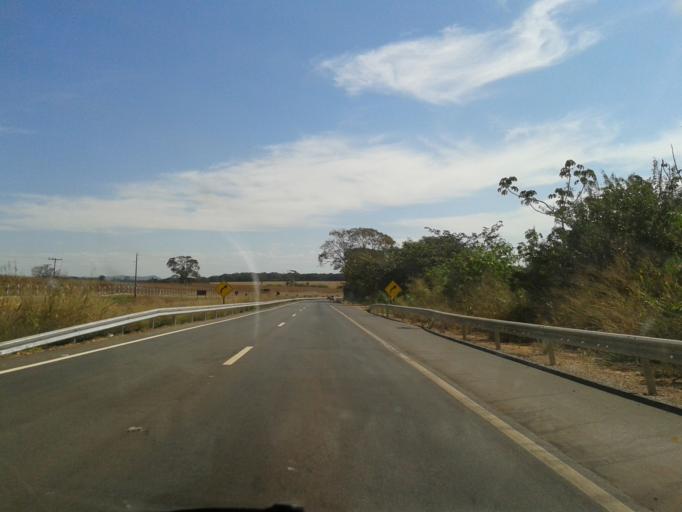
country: BR
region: Goias
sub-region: Itaberai
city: Itaberai
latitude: -16.0217
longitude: -49.8365
